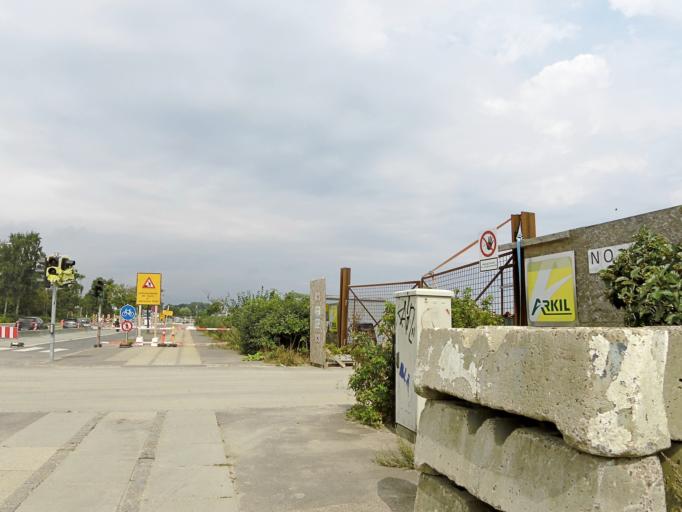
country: DK
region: Capital Region
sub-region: Gentofte Kommune
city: Charlottenlund
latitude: 55.7639
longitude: 12.5989
